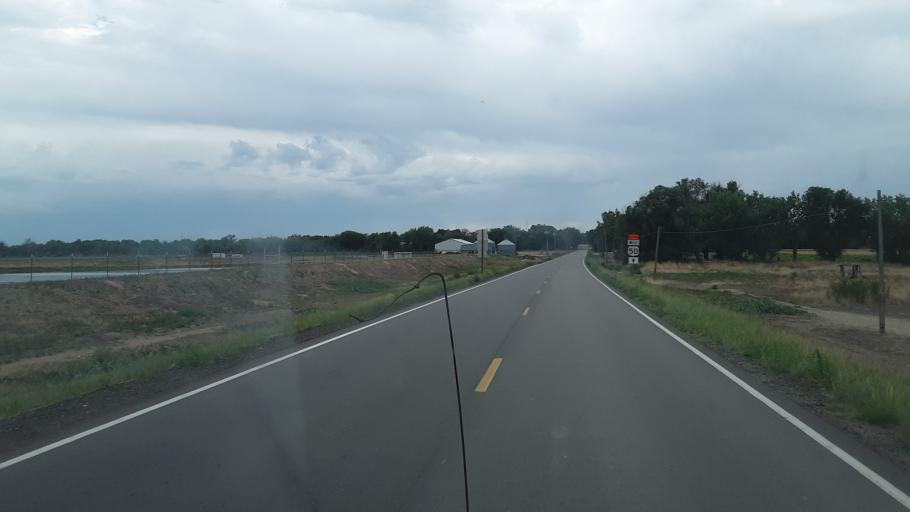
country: US
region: Colorado
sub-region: Otero County
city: Fowler
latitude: 38.1398
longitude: -104.0229
